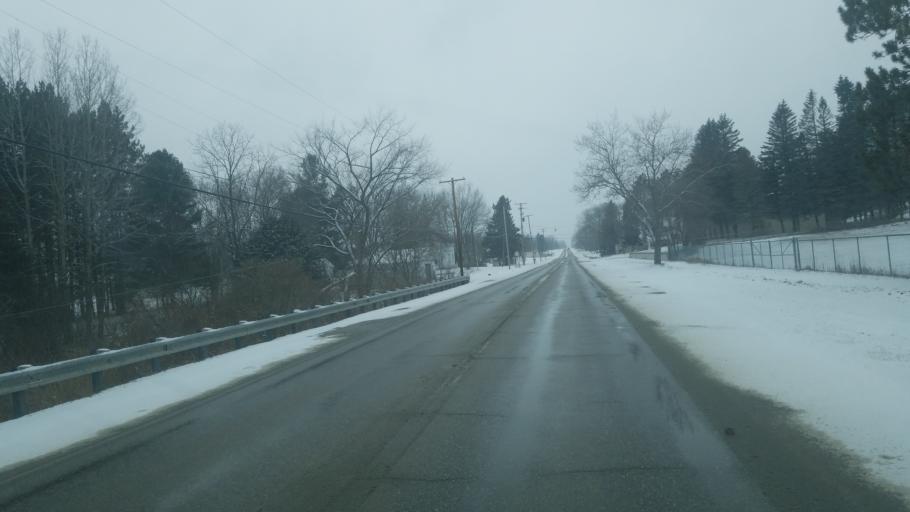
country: US
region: Michigan
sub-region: Osceola County
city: Evart
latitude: 44.1025
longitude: -85.1540
